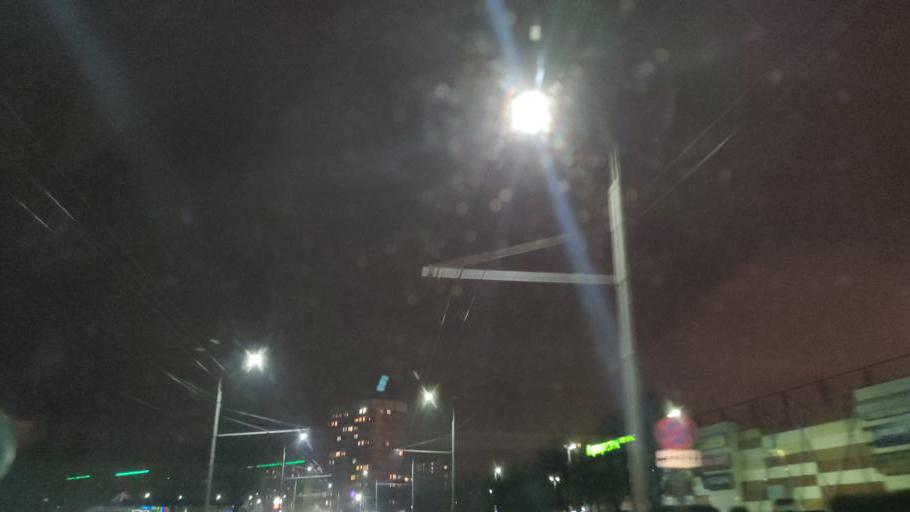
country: RU
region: Moskovskaya
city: Dubrovitsy
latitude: 55.4272
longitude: 37.5056
